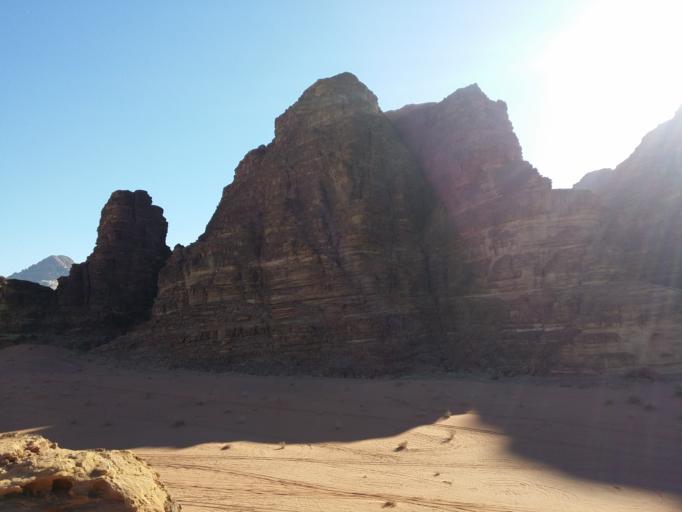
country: JO
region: Ma'an
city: Al Quwayrah
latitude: 29.6351
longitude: 35.4595
